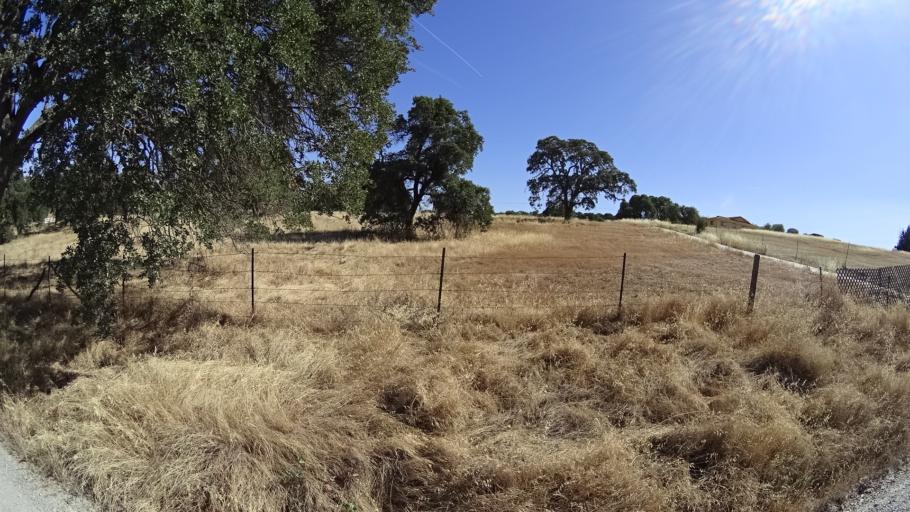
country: US
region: California
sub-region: Amador County
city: Jackson
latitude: 38.2593
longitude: -120.7691
